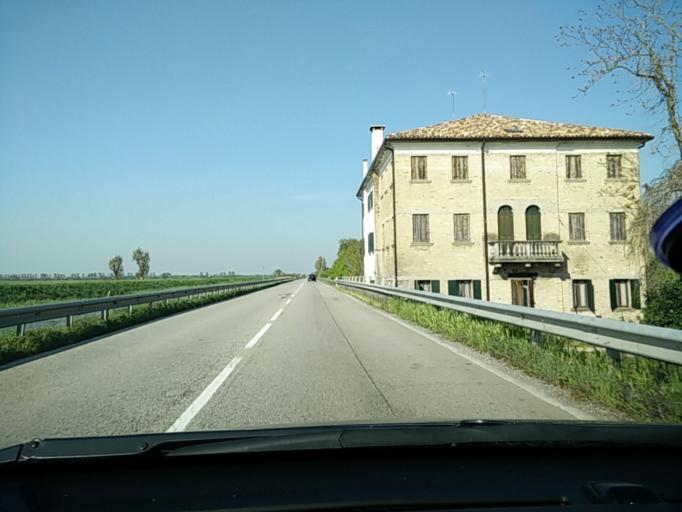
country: IT
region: Veneto
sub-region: Provincia di Venezia
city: Meolo
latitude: 45.5632
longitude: 12.4449
